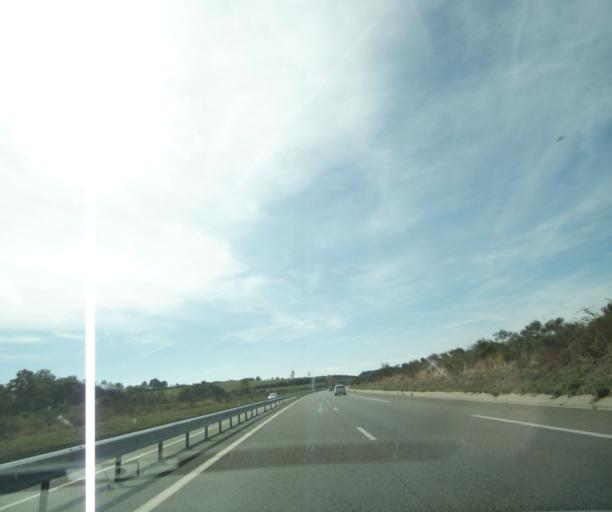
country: FR
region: Auvergne
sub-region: Departement du Puy-de-Dome
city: Saint-Ours
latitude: 45.8884
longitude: 2.9299
